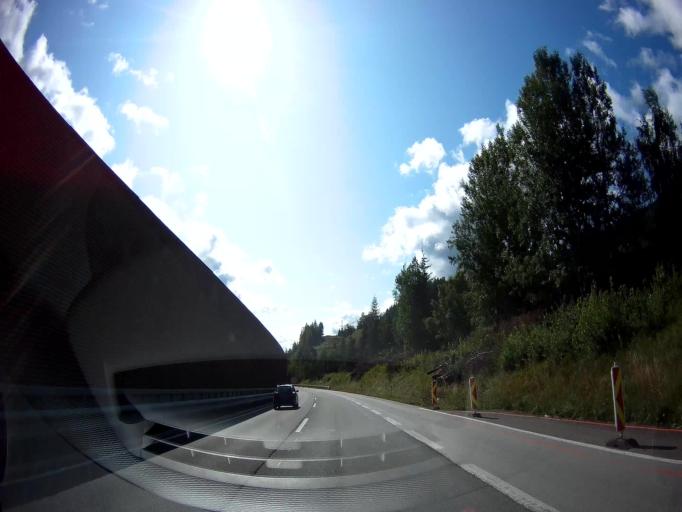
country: AT
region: Salzburg
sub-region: Politischer Bezirk Tamsweg
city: Zederhaus
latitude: 47.1275
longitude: 13.5527
